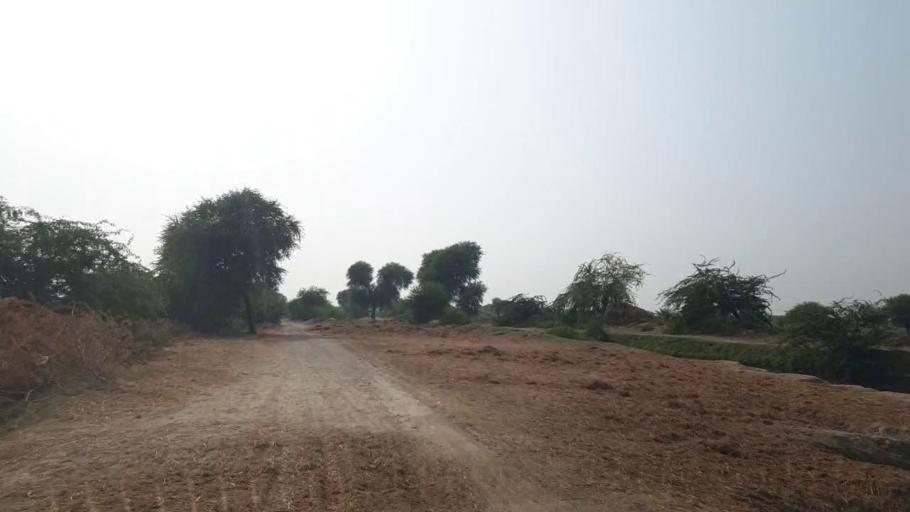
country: PK
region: Sindh
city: Rajo Khanani
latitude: 25.0364
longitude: 68.7858
